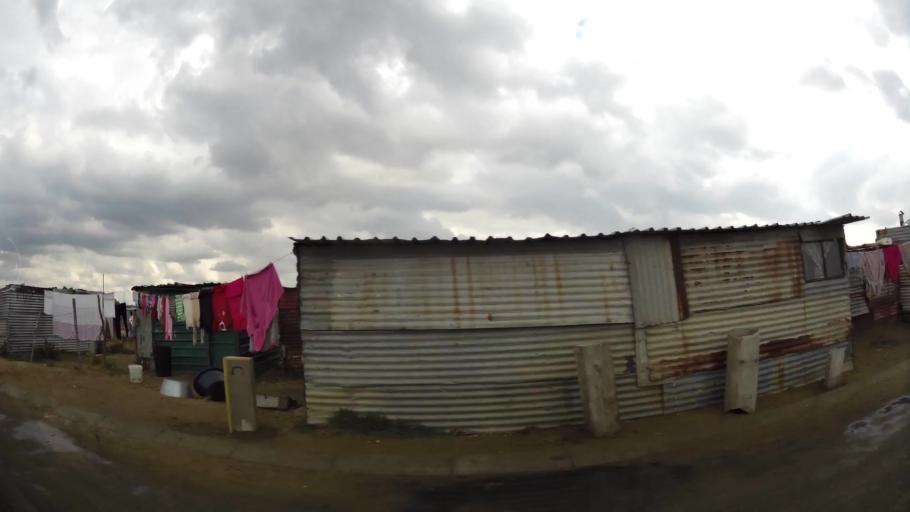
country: ZA
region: Orange Free State
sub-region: Fezile Dabi District Municipality
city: Sasolburg
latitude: -26.8603
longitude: 27.8727
